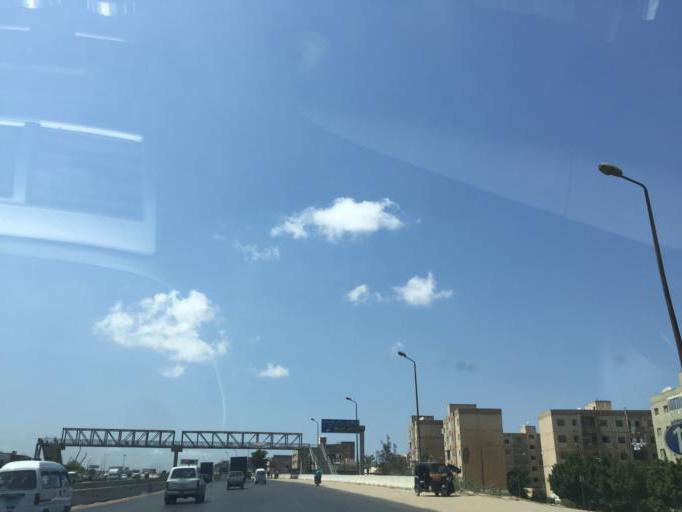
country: EG
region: Alexandria
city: Alexandria
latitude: 31.0249
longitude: 29.7925
